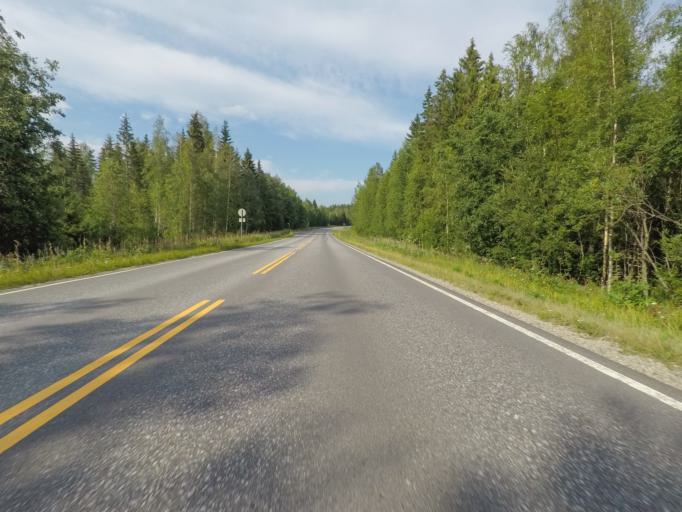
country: FI
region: Southern Savonia
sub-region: Savonlinna
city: Sulkava
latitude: 61.8649
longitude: 28.4727
